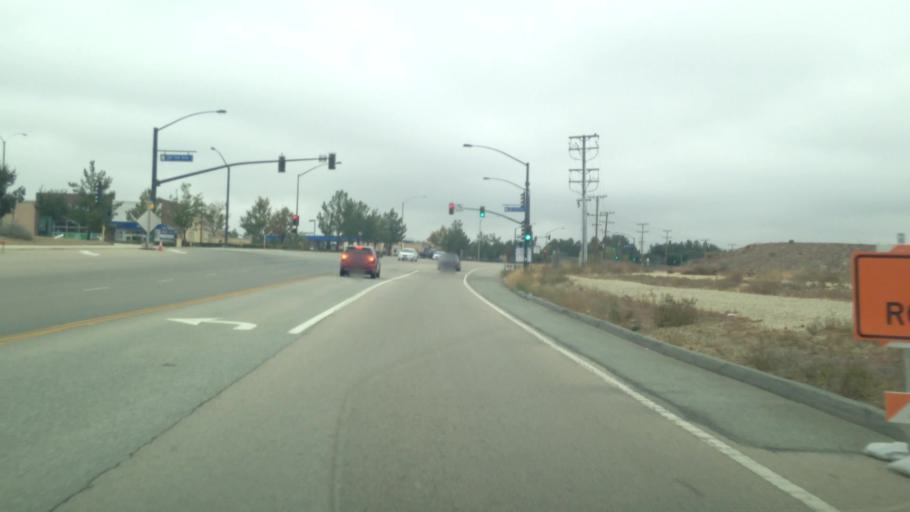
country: US
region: California
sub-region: Riverside County
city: Beaumont
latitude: 33.9462
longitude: -117.0003
